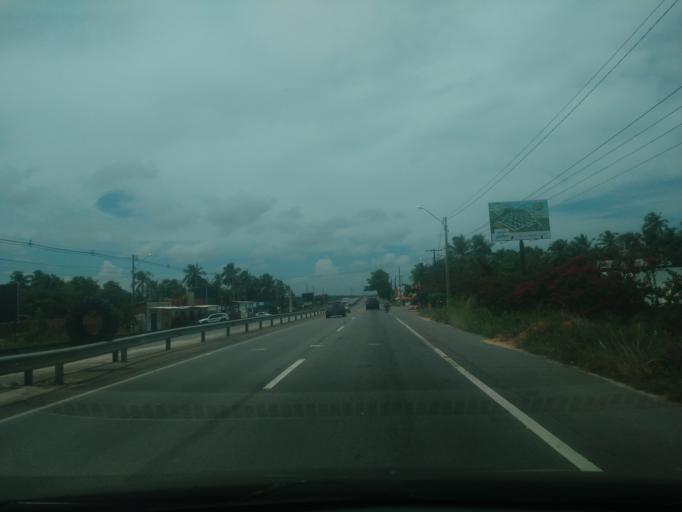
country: BR
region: Alagoas
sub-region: Marechal Deodoro
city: Marechal Deodoro
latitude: -9.7369
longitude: -35.8342
